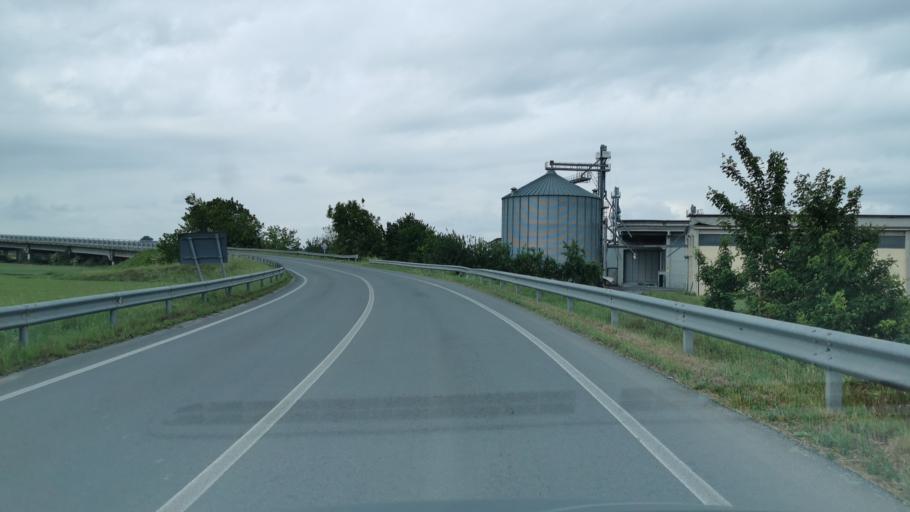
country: IT
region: Piedmont
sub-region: Provincia di Cuneo
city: Savigliano
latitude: 44.6404
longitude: 7.6441
